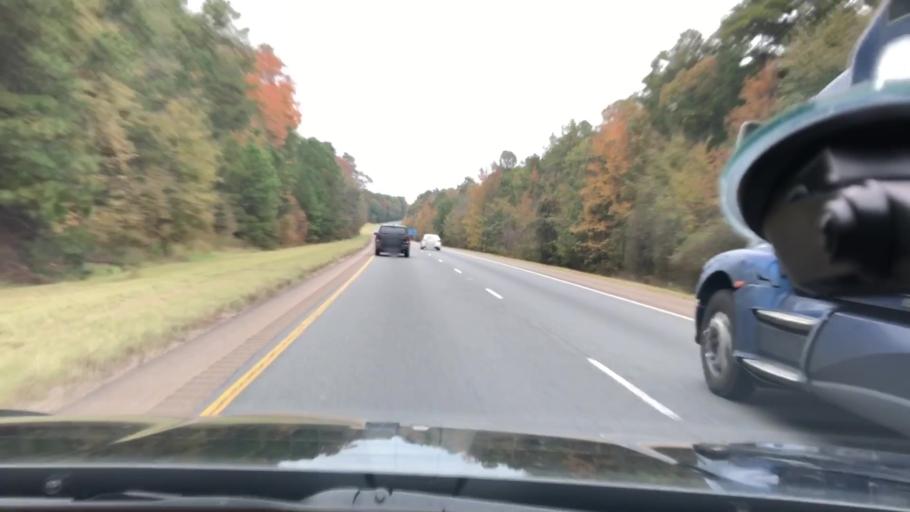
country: US
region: Arkansas
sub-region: Clark County
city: Gurdon
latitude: 33.9227
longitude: -93.2700
